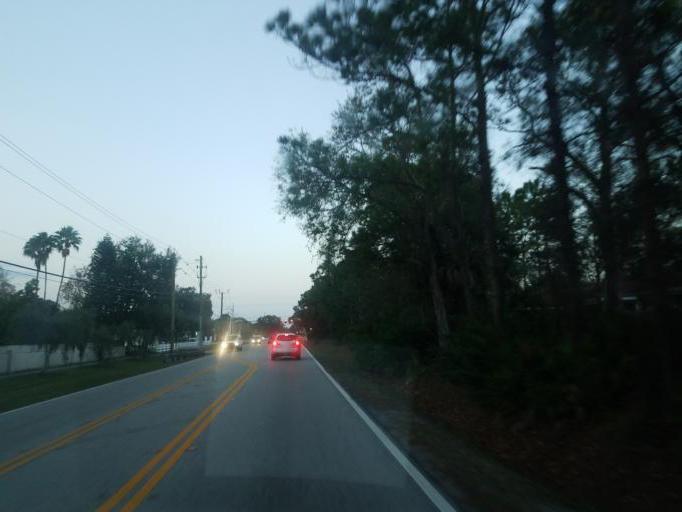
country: US
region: Florida
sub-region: Sarasota County
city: The Meadows
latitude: 27.3503
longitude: -82.4640
